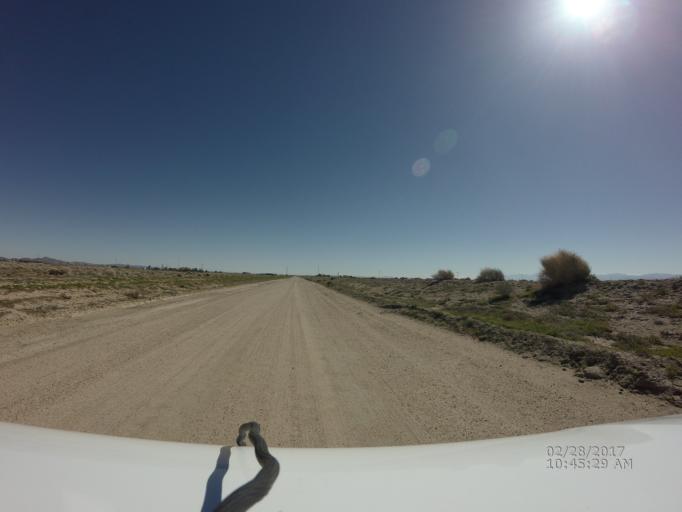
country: US
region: California
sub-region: Kern County
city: Rosamond
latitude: 34.8055
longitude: -118.2762
